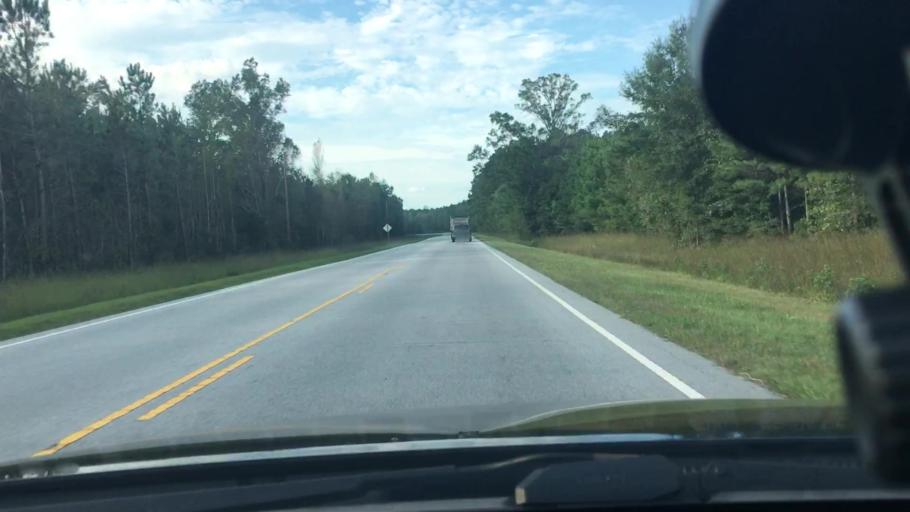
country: US
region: North Carolina
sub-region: Craven County
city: Vanceboro
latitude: 35.2963
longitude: -77.1308
